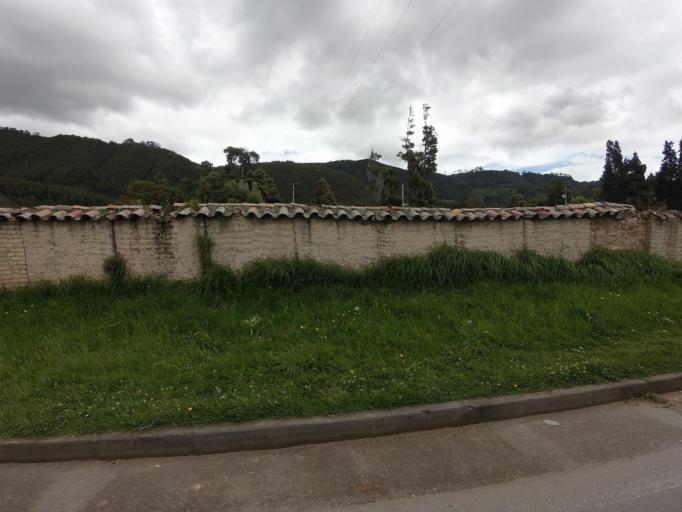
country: CO
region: Cundinamarca
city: Cajica
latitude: 4.9419
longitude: -74.0308
